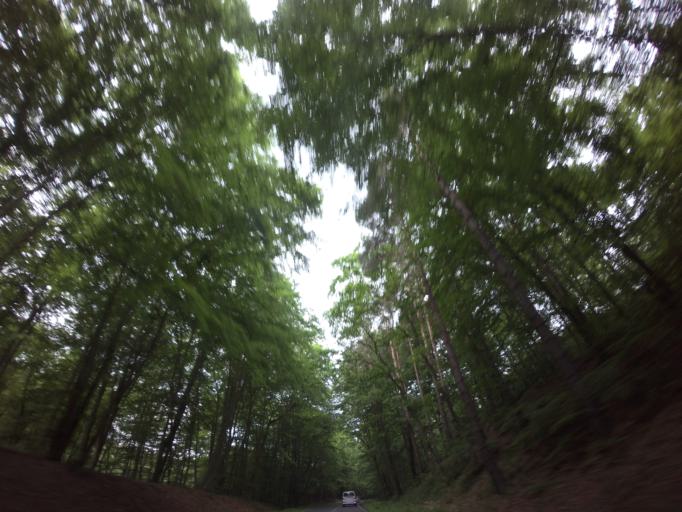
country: PL
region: West Pomeranian Voivodeship
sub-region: Powiat stargardzki
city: Suchan
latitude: 53.2631
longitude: 15.3302
